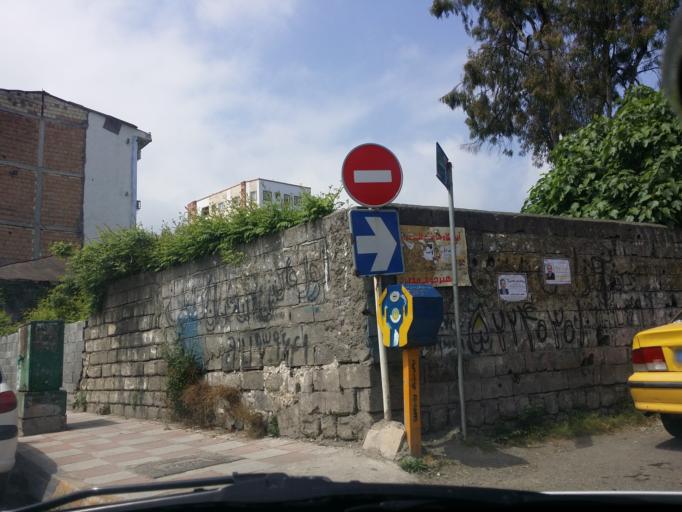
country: IR
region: Mazandaran
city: Chalus
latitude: 36.6548
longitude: 51.4175
